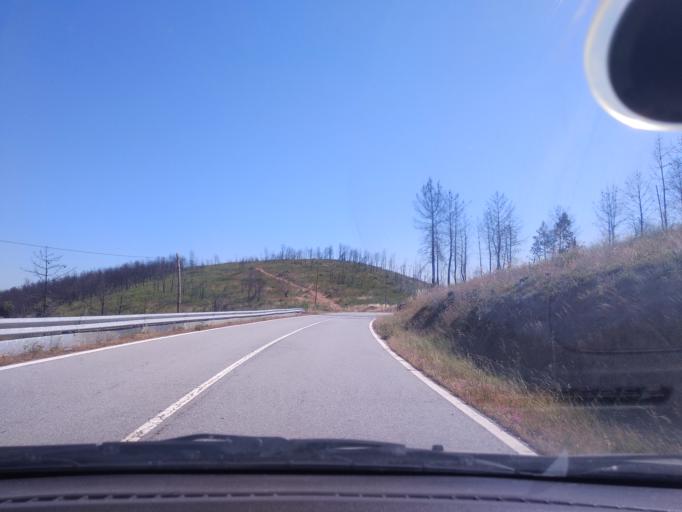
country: PT
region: Portalegre
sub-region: Nisa
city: Nisa
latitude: 39.6241
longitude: -7.6649
